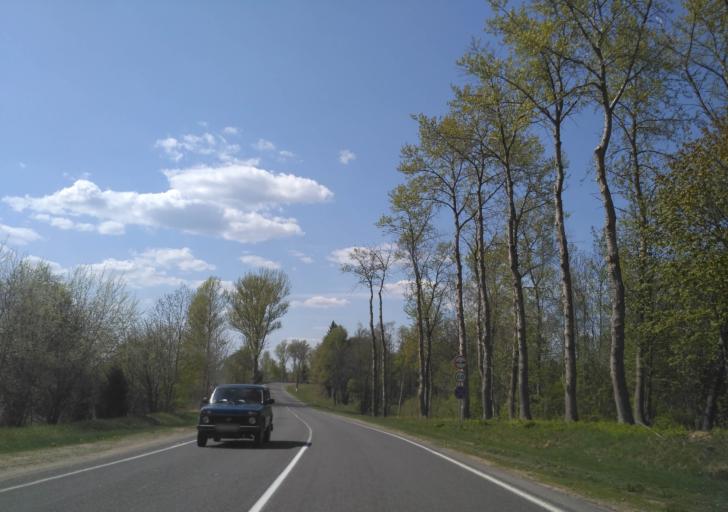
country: BY
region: Minsk
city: Narach
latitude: 54.8972
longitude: 26.7578
